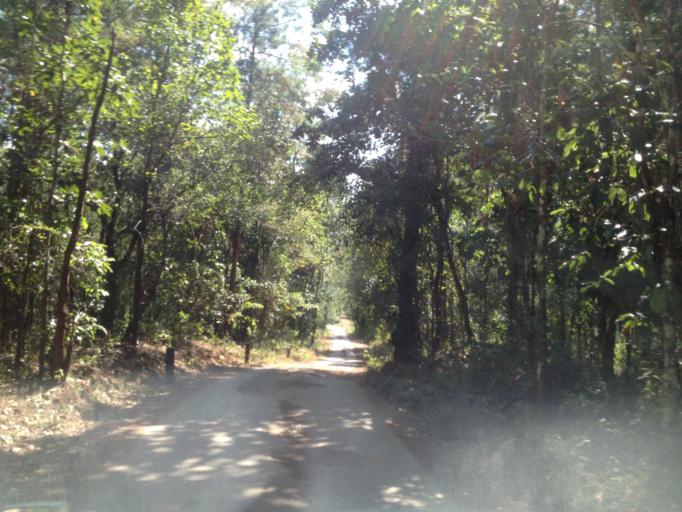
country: TH
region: Mae Hong Son
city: Ban Huai I Huak
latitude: 18.1074
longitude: 98.1716
